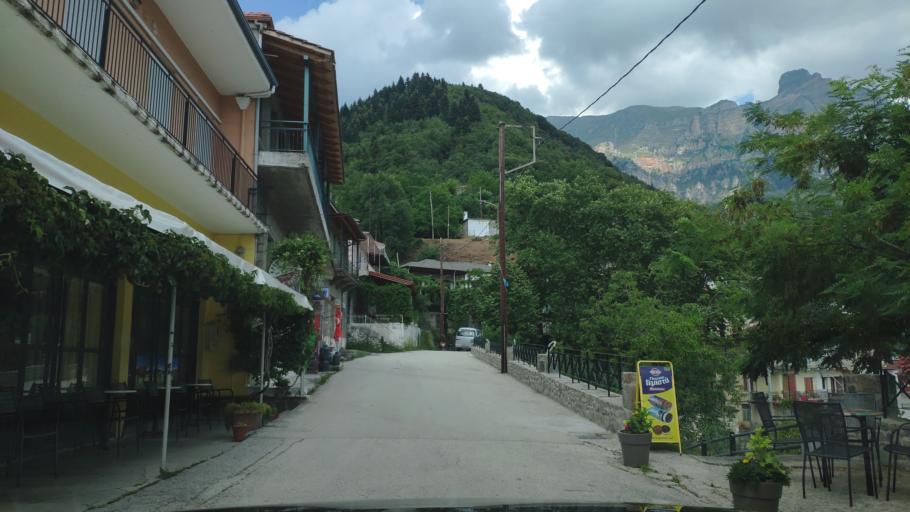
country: GR
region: Epirus
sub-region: Nomos Ioanninon
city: Pramanta
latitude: 39.4740
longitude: 21.0796
